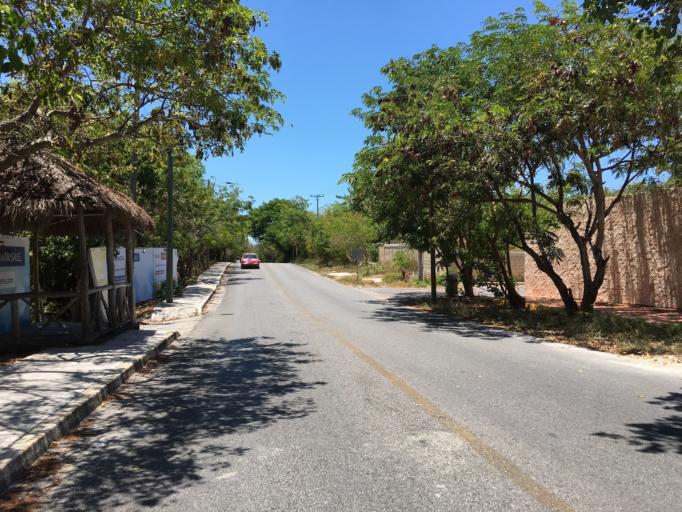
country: MX
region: Quintana Roo
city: Isla Mujeres
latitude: 21.2165
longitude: -86.7255
